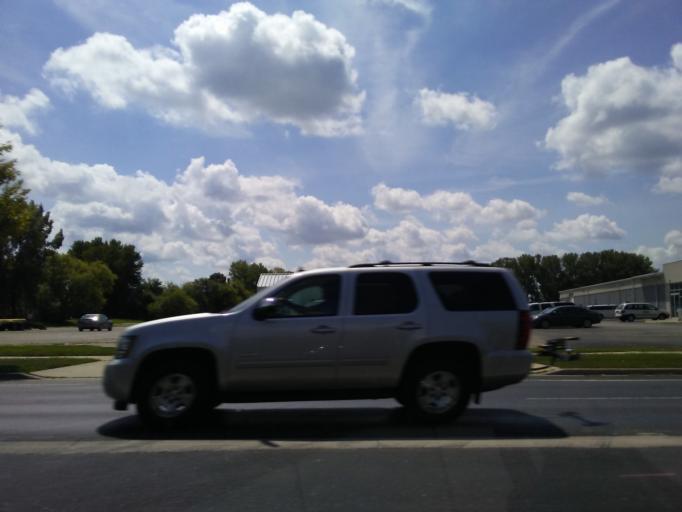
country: US
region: Wisconsin
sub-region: Dane County
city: Verona
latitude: 42.9887
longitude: -89.5439
